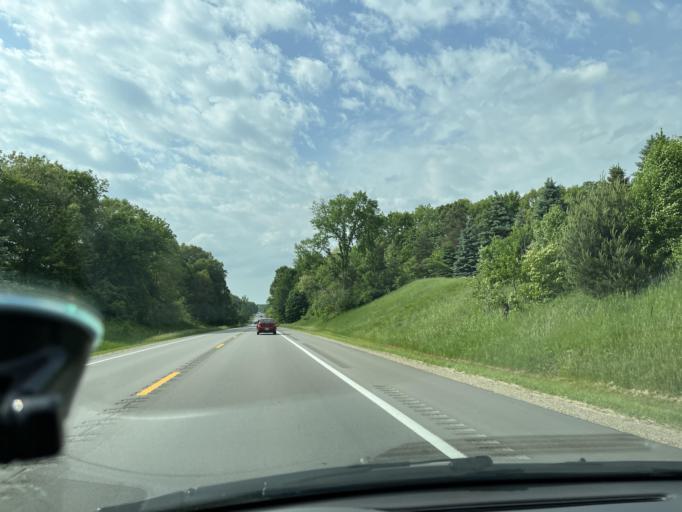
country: US
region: Michigan
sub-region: Barry County
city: Middleville
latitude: 42.7280
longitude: -85.4782
